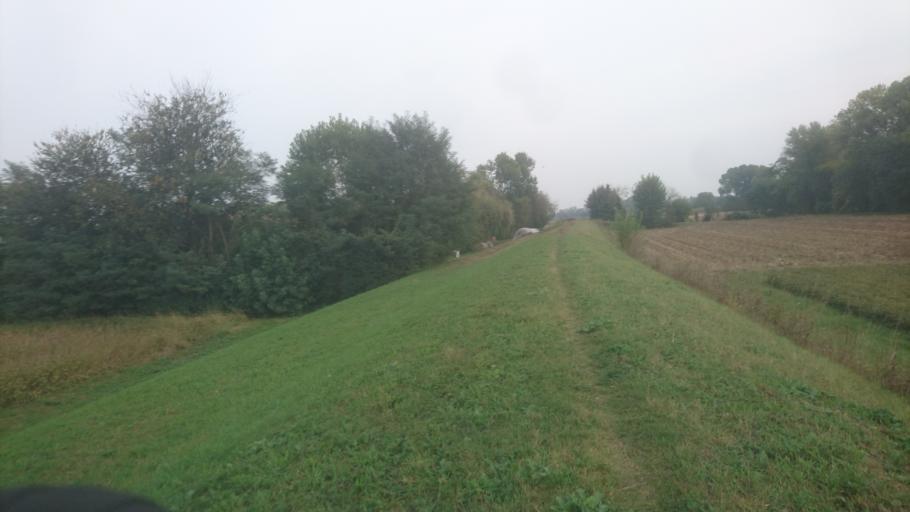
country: IT
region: Veneto
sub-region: Provincia di Padova
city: Cervarese Santa Croce
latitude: 45.4229
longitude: 11.7064
